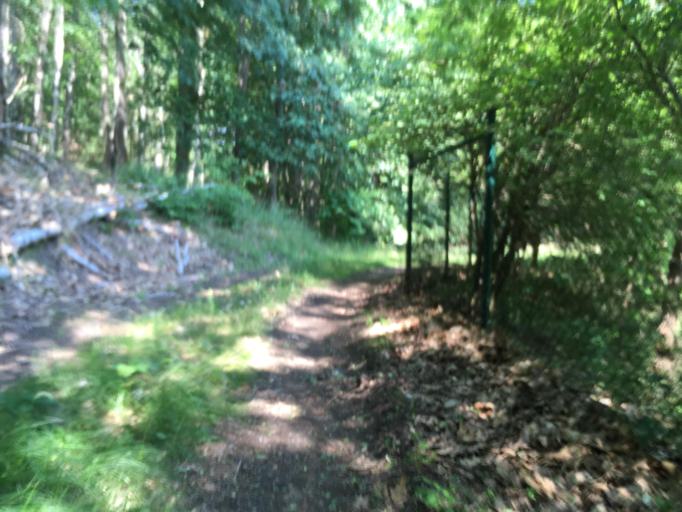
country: DE
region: Brandenburg
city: Marienwerder
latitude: 52.9212
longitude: 13.6595
